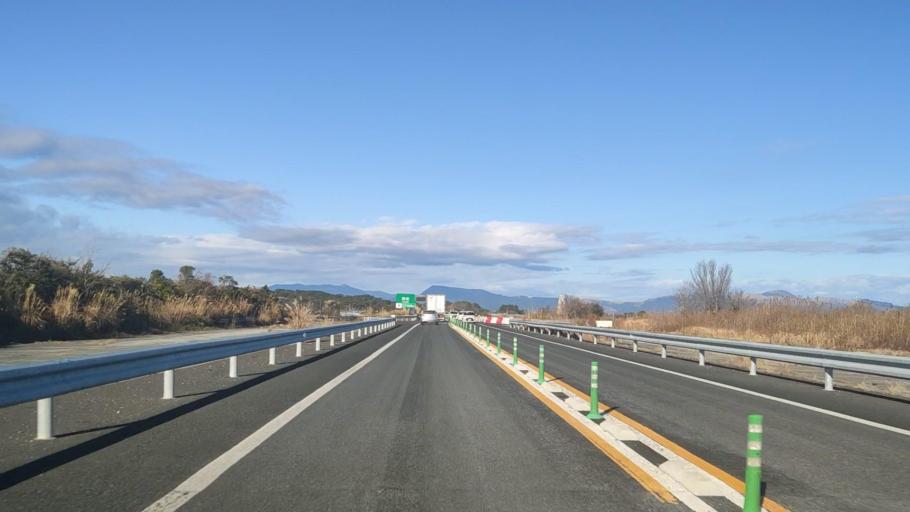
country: JP
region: Fukuoka
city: Tsuiki
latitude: 33.6591
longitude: 131.0211
